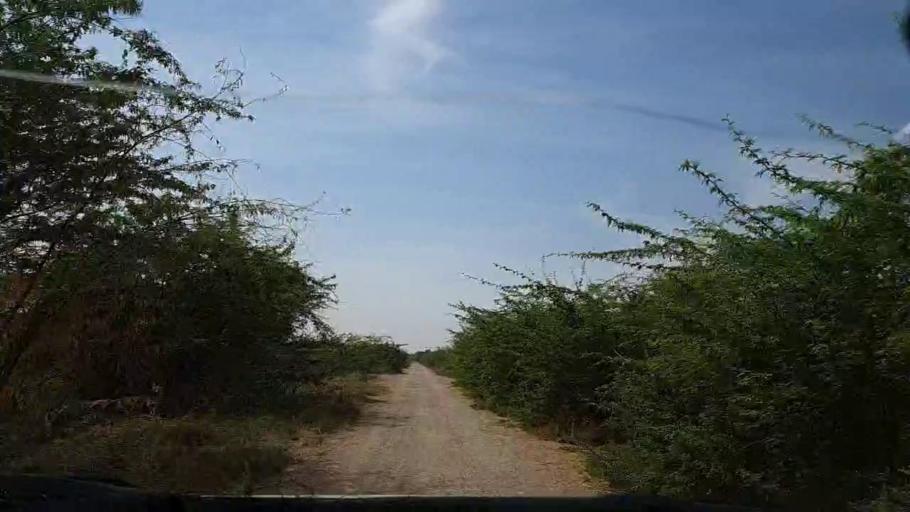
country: PK
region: Sindh
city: Pithoro
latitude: 25.4829
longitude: 69.4460
